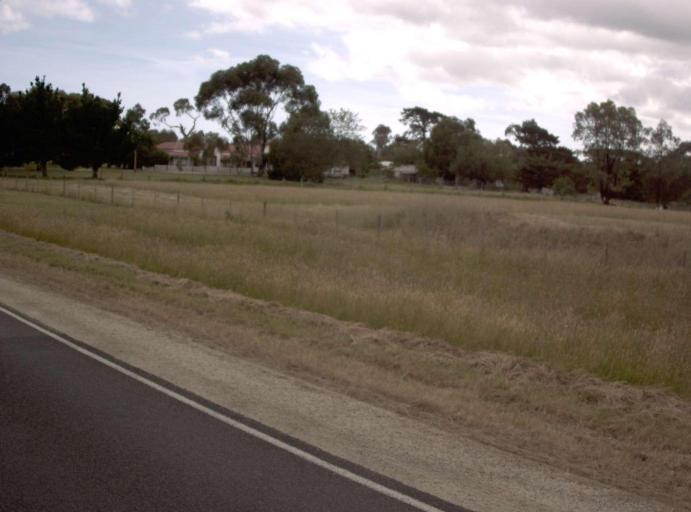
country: AU
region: Victoria
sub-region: Wellington
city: Sale
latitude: -38.1819
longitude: 147.0906
